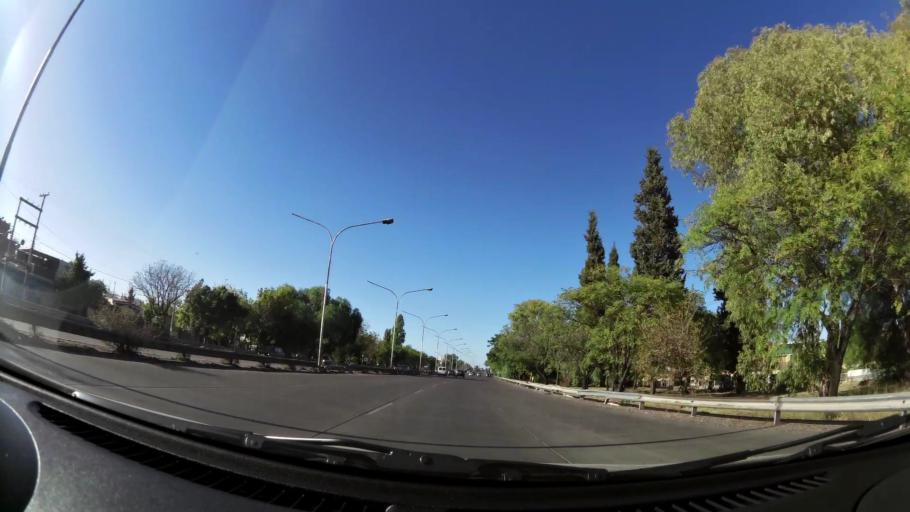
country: AR
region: Mendoza
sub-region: Departamento de Godoy Cruz
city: Godoy Cruz
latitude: -32.9149
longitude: -68.8375
